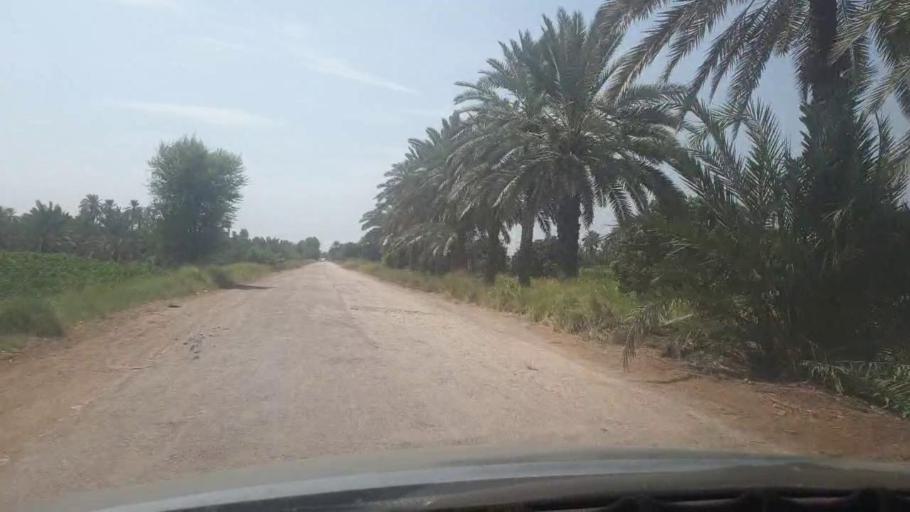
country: PK
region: Sindh
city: Bozdar
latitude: 27.2014
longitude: 68.5834
